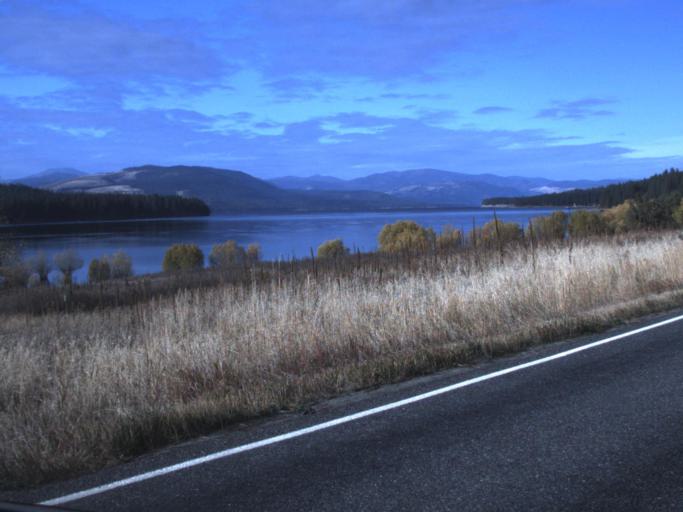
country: US
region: Washington
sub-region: Stevens County
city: Kettle Falls
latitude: 48.2583
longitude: -118.1319
